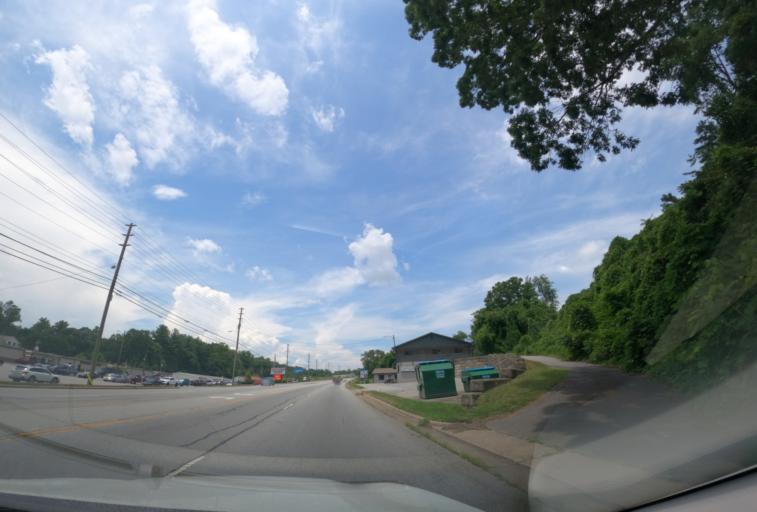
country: US
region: North Carolina
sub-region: Buncombe County
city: Bent Creek
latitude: 35.5168
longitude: -82.6044
